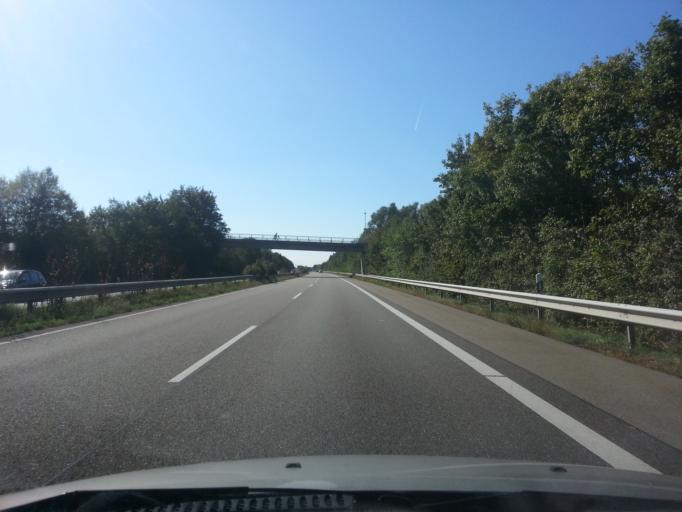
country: DE
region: Baden-Wuerttemberg
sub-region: Karlsruhe Region
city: Hockenheim
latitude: 49.3172
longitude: 8.5362
